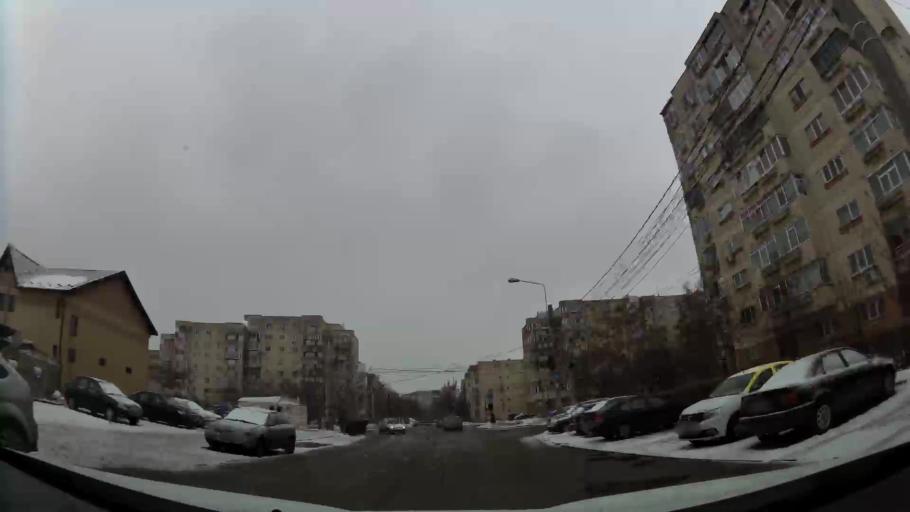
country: RO
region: Prahova
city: Ploiesti
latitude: 44.9312
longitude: 25.9982
